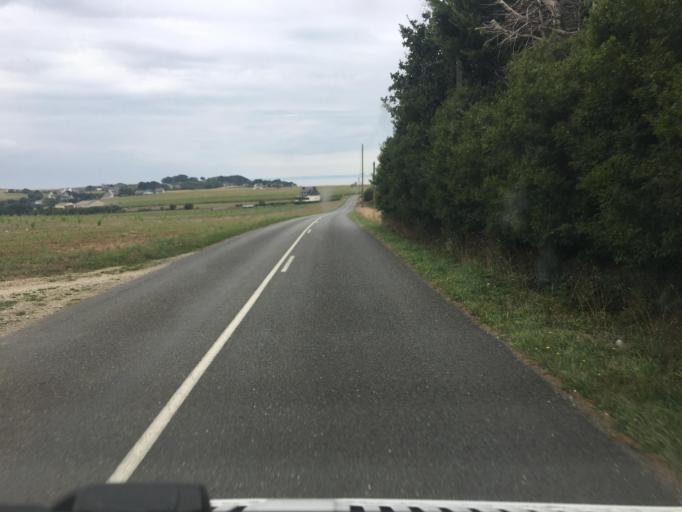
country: FR
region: Brittany
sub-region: Departement du Finistere
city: Plonevez-Porzay
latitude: 48.1294
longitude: -4.2490
